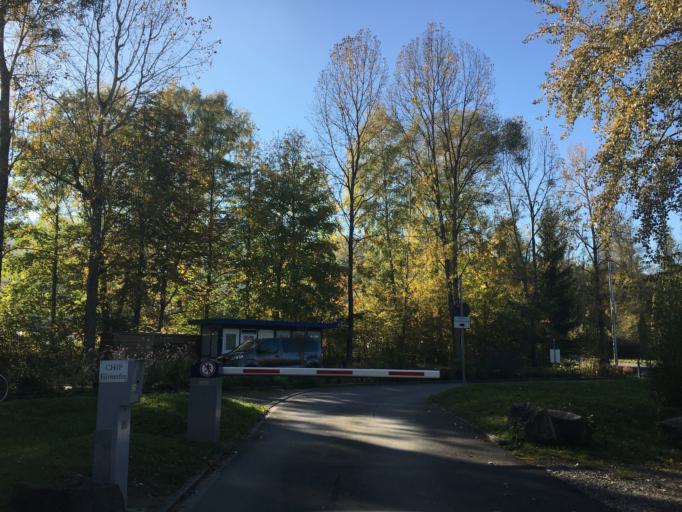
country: DE
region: Baden-Wuerttemberg
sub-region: Freiburg Region
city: Konstanz
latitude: 47.7000
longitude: 9.1837
